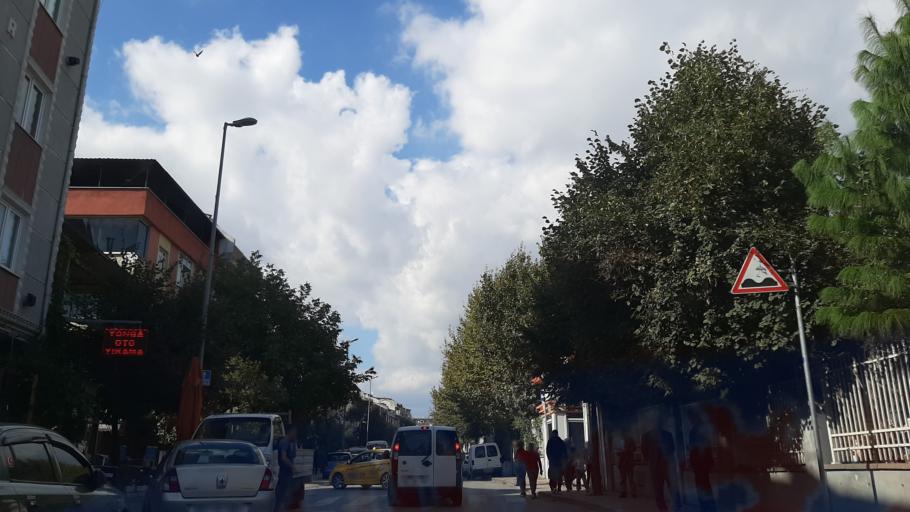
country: TR
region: Istanbul
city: Esenyurt
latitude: 41.0350
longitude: 28.6593
